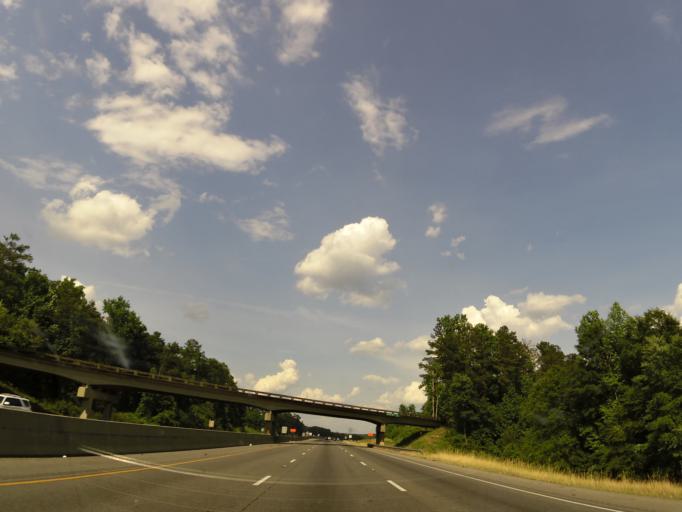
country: US
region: Alabama
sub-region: Tuscaloosa County
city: Coaling
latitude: 33.1806
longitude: -87.3709
